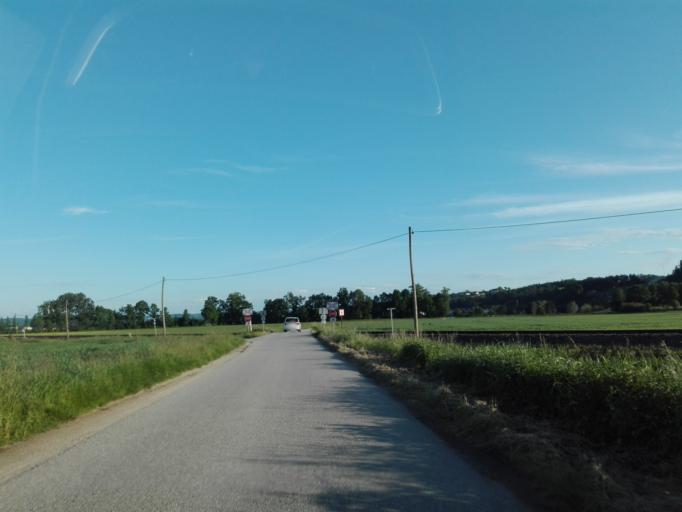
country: AT
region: Upper Austria
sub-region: Politischer Bezirk Urfahr-Umgebung
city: Feldkirchen an der Donau
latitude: 48.3339
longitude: 14.0012
